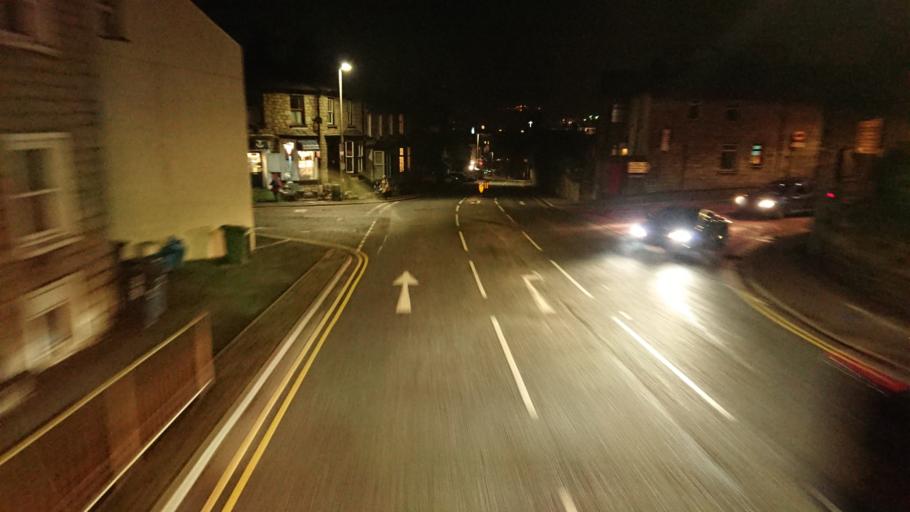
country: GB
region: England
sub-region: Cumbria
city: Kendal
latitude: 54.3329
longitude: -2.7536
